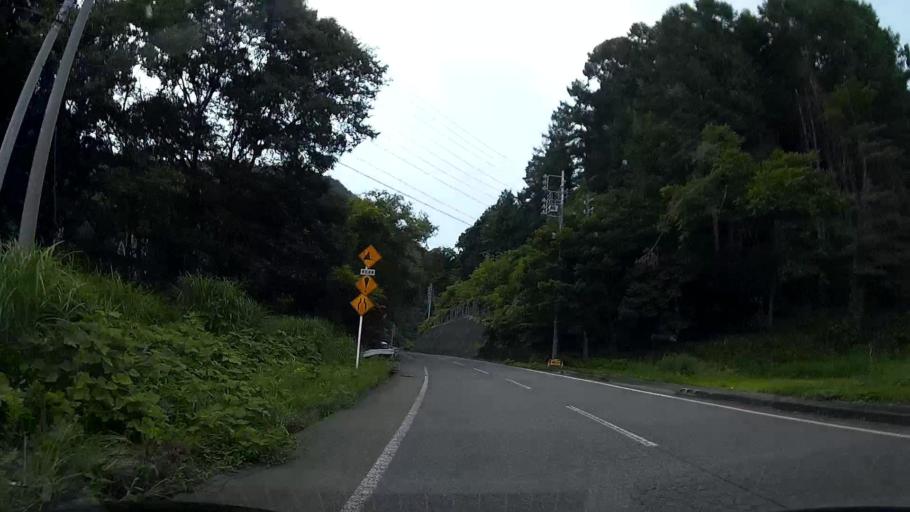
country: JP
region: Nagano
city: Iiyama
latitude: 36.8269
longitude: 138.4222
